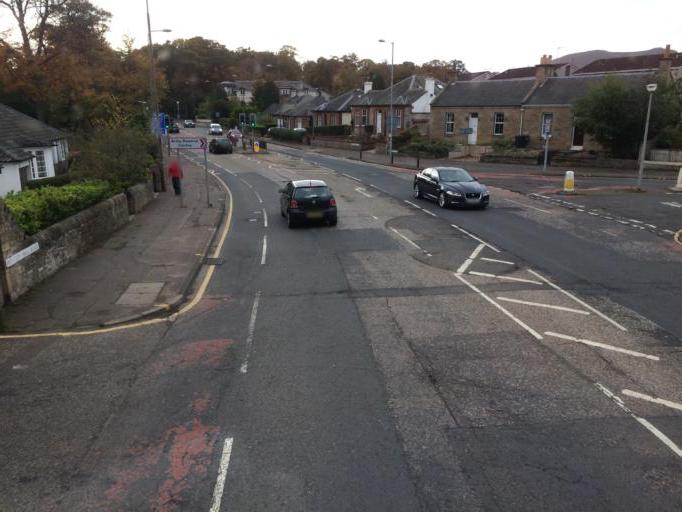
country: GB
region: Scotland
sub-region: Midlothian
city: Loanhead
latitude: 55.9053
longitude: -3.1655
